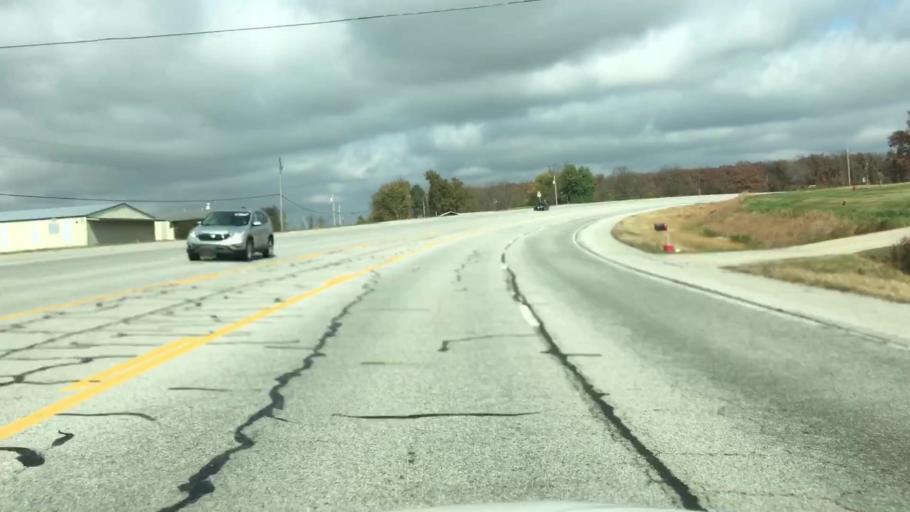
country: US
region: Arkansas
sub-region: Benton County
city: Gentry
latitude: 36.2296
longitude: -94.4950
